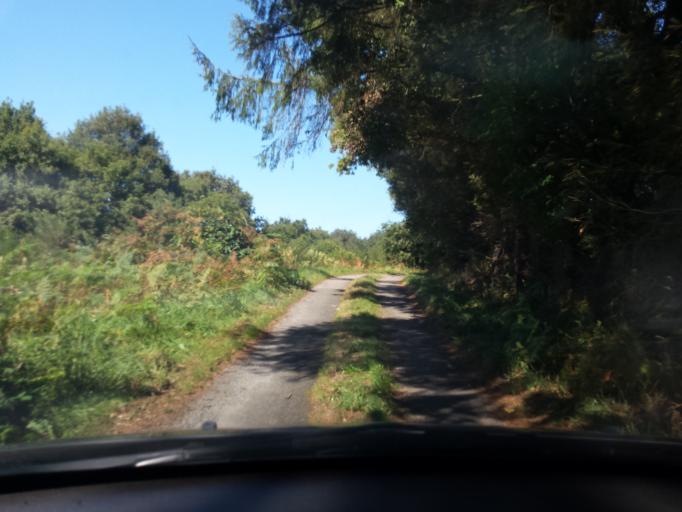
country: FR
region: Brittany
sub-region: Departement des Cotes-d'Armor
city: Plounevez-Quintin
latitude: 48.3377
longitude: -3.2502
